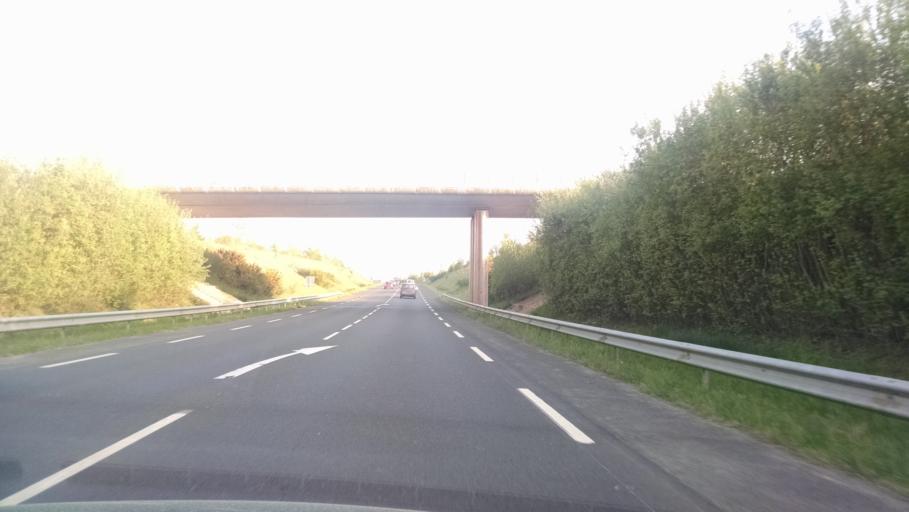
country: FR
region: Pays de la Loire
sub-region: Departement de la Loire-Atlantique
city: Clisson
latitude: 47.0899
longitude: -1.2636
